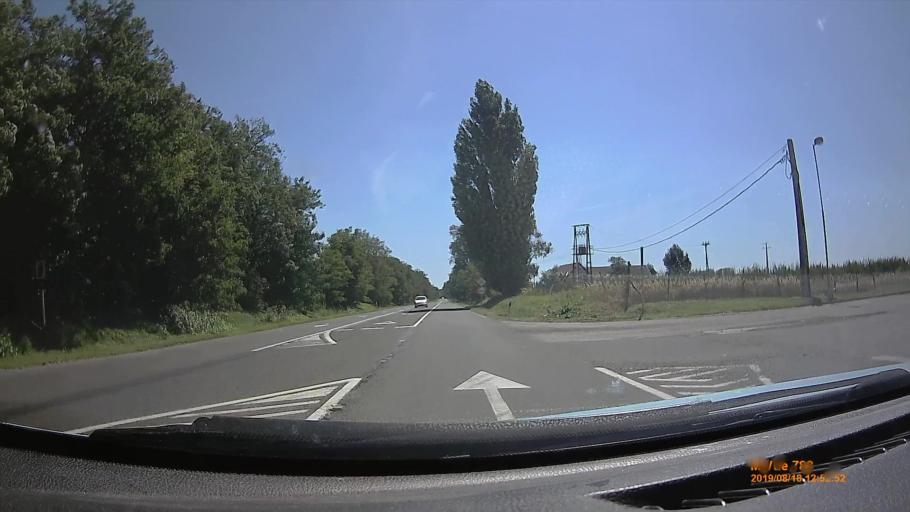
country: HU
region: Fejer
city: Aba
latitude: 47.0581
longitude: 18.5199
